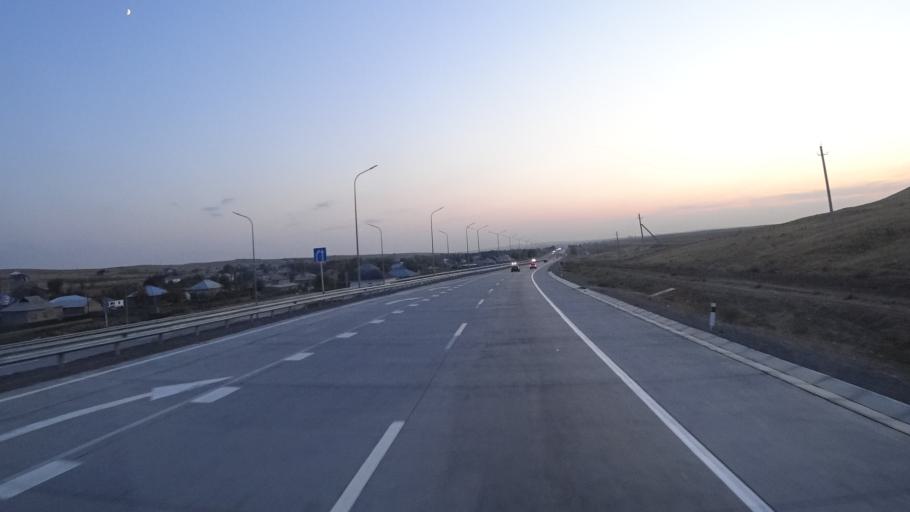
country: KZ
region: Ongtustik Qazaqstan
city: Qazyqurt
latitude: 41.8957
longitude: 69.4526
